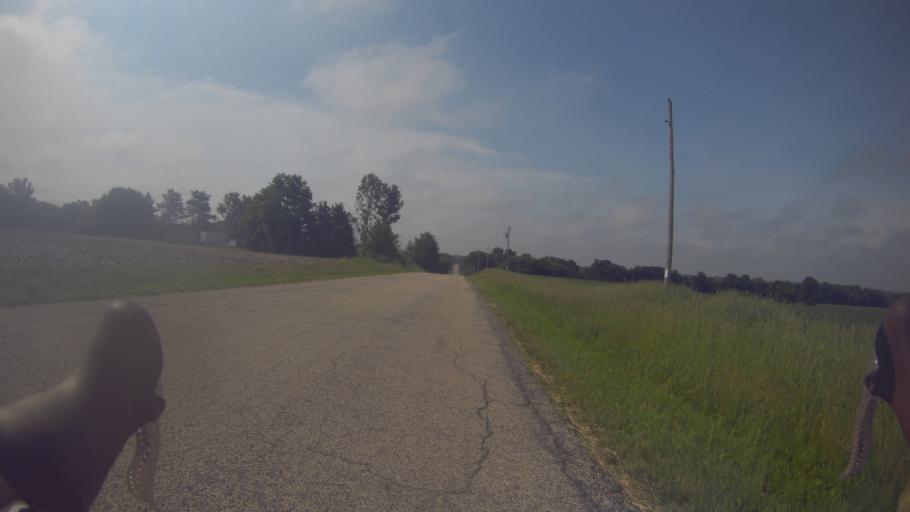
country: US
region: Wisconsin
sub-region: Dane County
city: Stoughton
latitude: 42.9583
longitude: -89.1810
